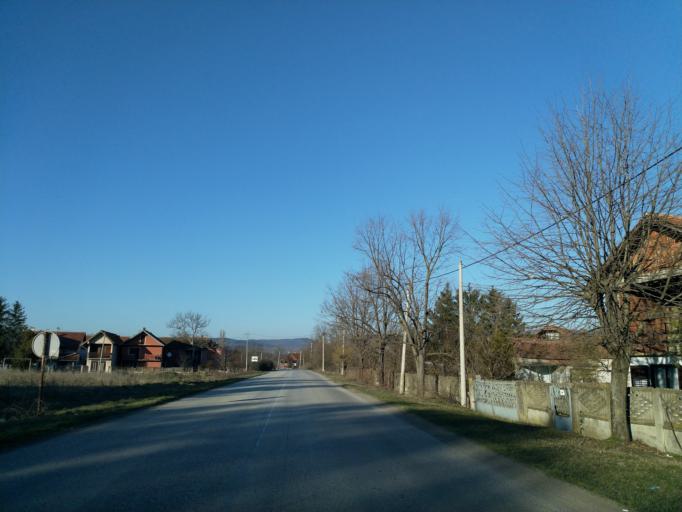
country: RS
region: Central Serbia
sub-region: Pomoravski Okrug
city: Paracin
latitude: 43.8863
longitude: 21.4814
